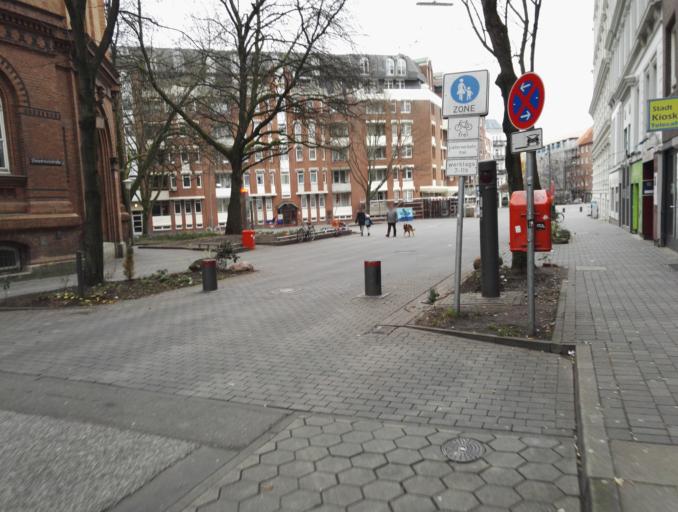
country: DE
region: Hamburg
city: St. Georg
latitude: 53.5545
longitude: 10.0105
